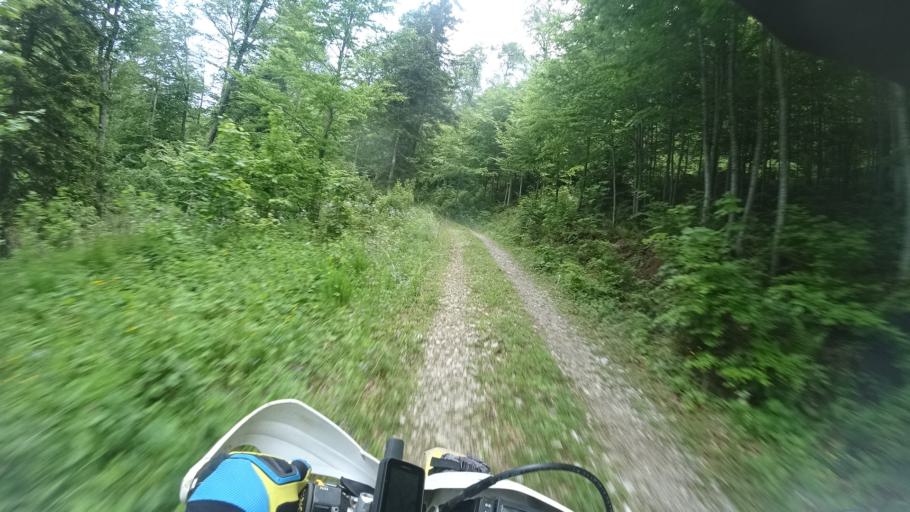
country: HR
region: Zadarska
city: Gracac
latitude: 44.4723
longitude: 15.8894
